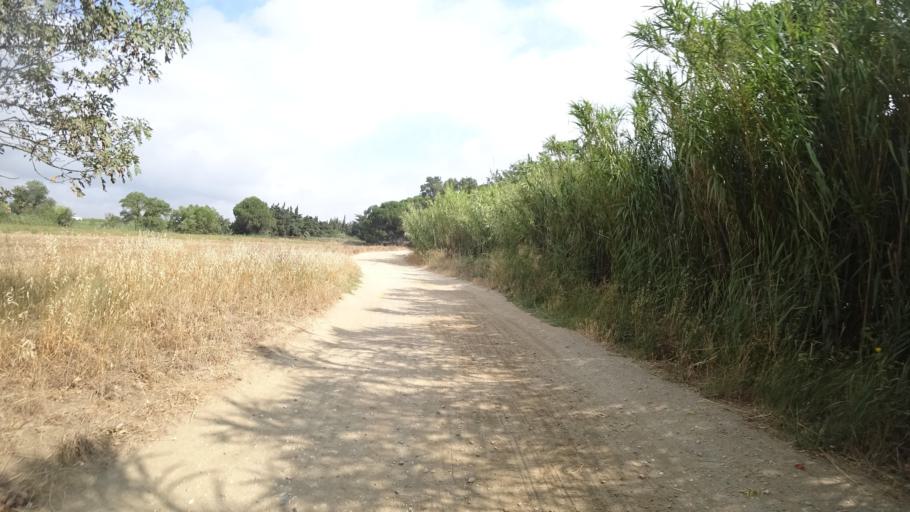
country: FR
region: Languedoc-Roussillon
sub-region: Departement des Pyrenees-Orientales
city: Sainte-Marie-Plage
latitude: 42.7177
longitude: 3.0301
